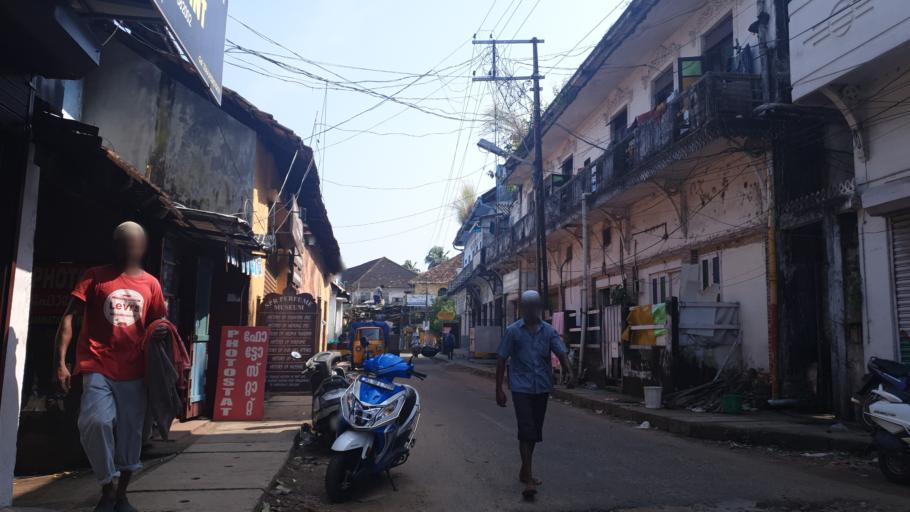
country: IN
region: Kerala
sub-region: Ernakulam
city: Cochin
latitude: 9.9630
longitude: 76.2572
